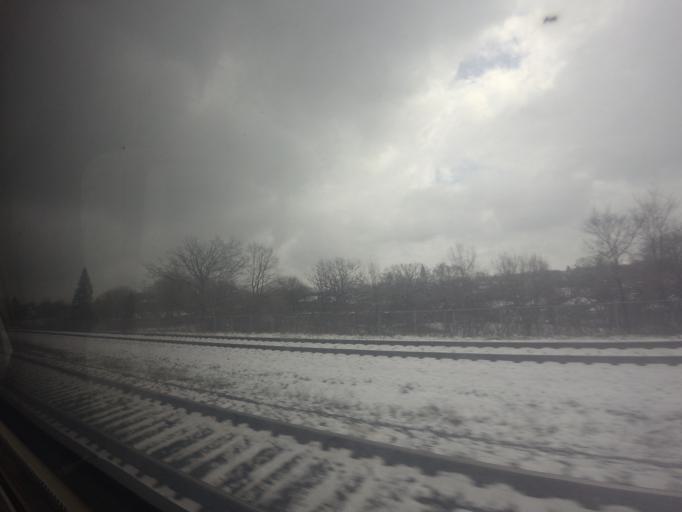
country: CA
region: Ontario
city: Scarborough
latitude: 43.6943
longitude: -79.2720
